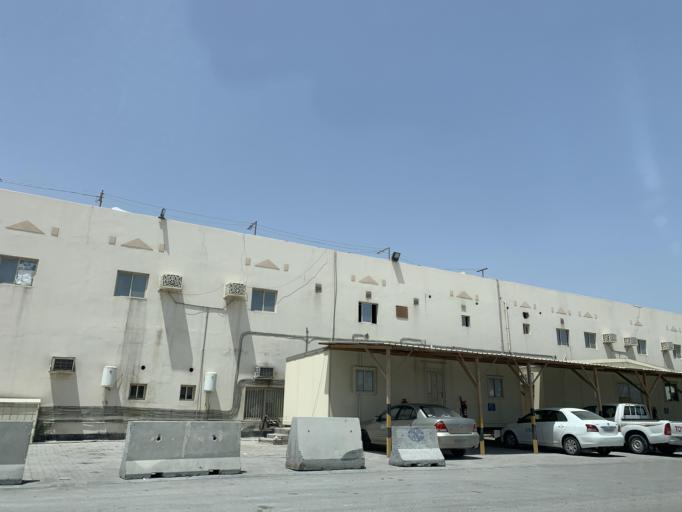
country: BH
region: Northern
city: Sitrah
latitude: 26.1474
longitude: 50.5984
